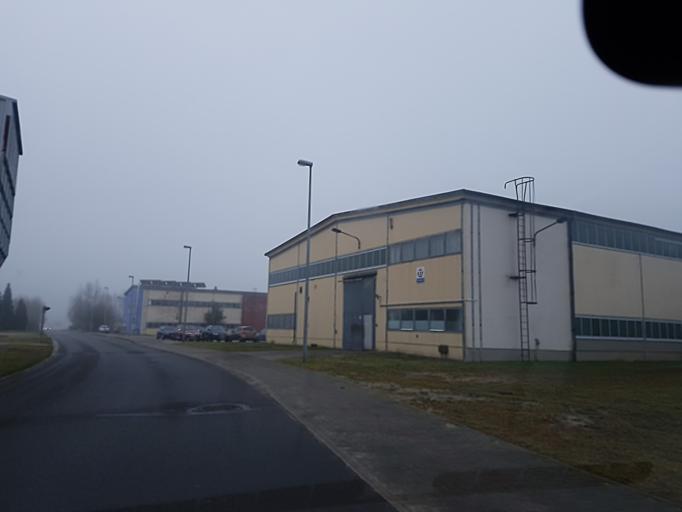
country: DE
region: Brandenburg
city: Finsterwalde
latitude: 51.6342
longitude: 13.7303
